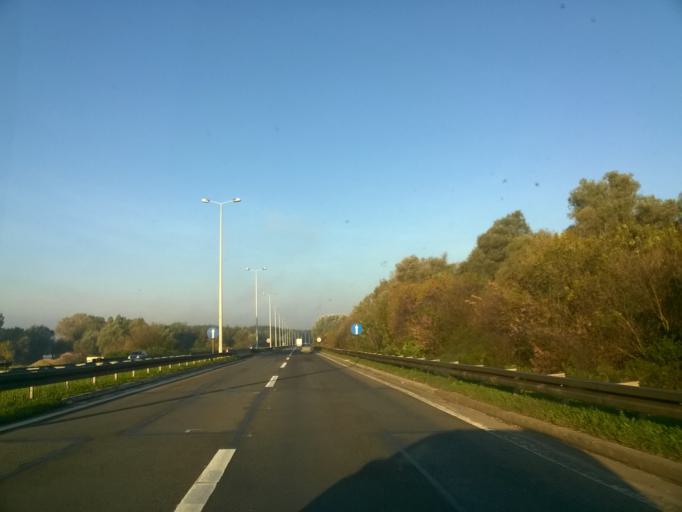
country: RS
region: Autonomna Pokrajina Vojvodina
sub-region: Juznobanatski Okrug
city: Pancevo
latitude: 44.8582
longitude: 20.6075
